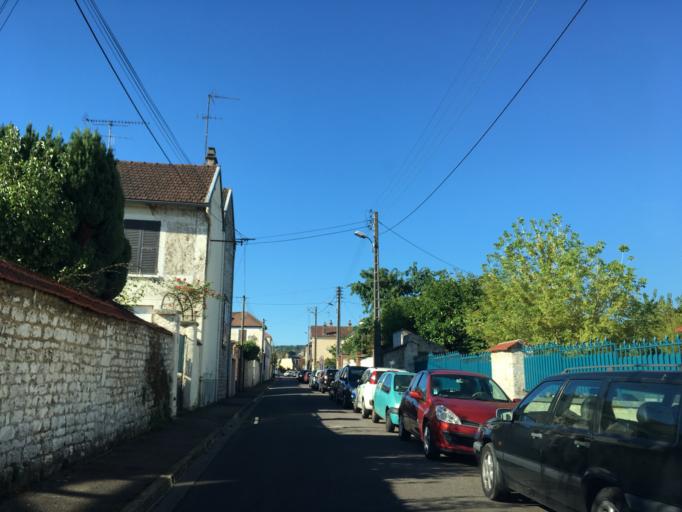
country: FR
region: Haute-Normandie
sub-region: Departement de l'Eure
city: Vernon
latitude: 49.0911
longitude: 1.4767
